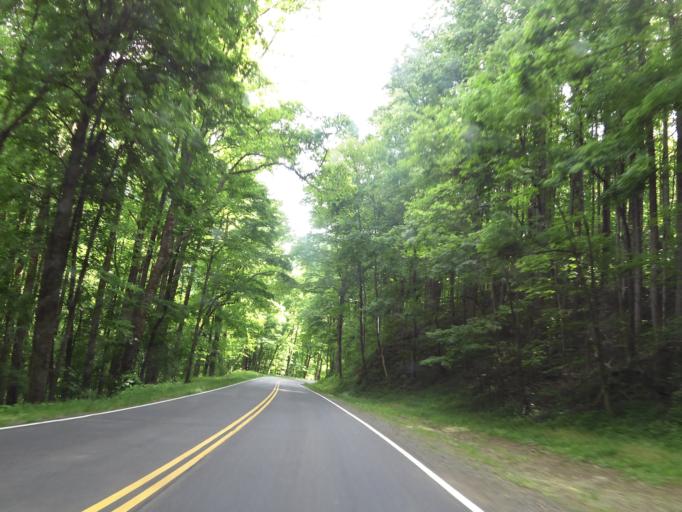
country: US
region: Tennessee
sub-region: Sevier County
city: Gatlinburg
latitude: 35.6406
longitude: -83.4837
